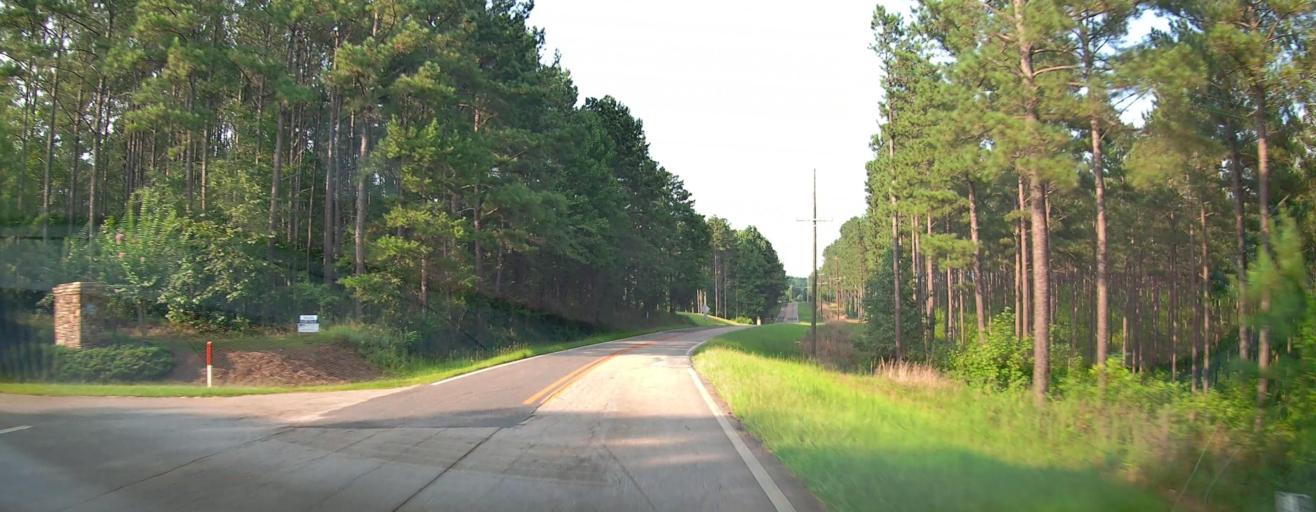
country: US
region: Georgia
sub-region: Monroe County
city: Forsyth
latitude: 32.9678
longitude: -83.8110
